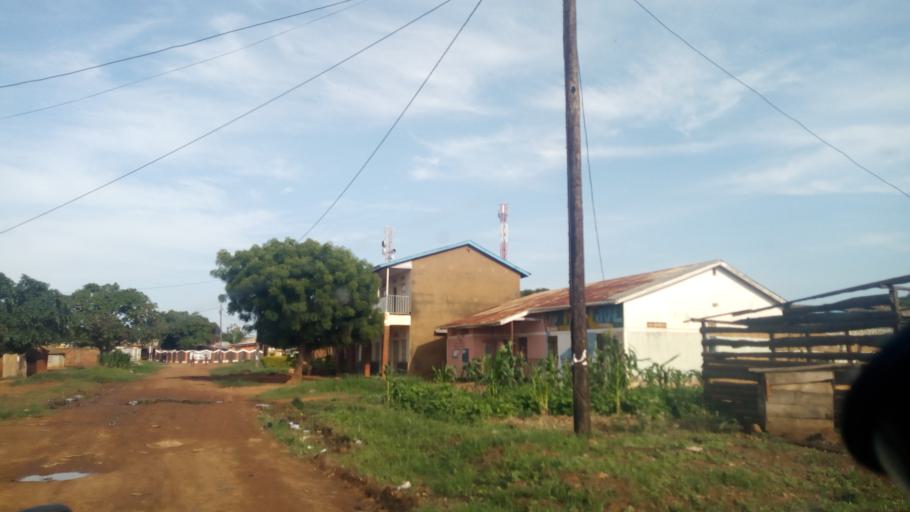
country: UG
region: Northern Region
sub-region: Gulu District
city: Gulu
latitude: 2.7675
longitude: 32.3011
